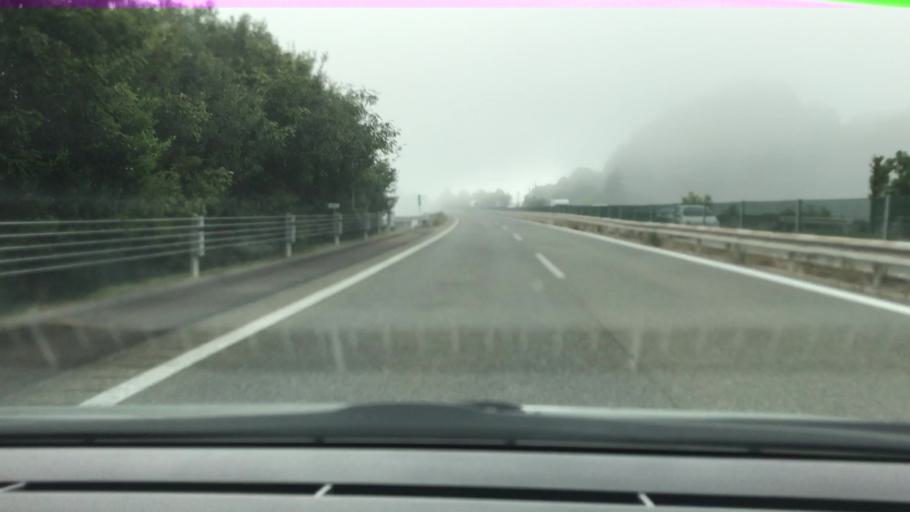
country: JP
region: Hyogo
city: Sasayama
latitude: 35.0716
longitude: 135.1737
